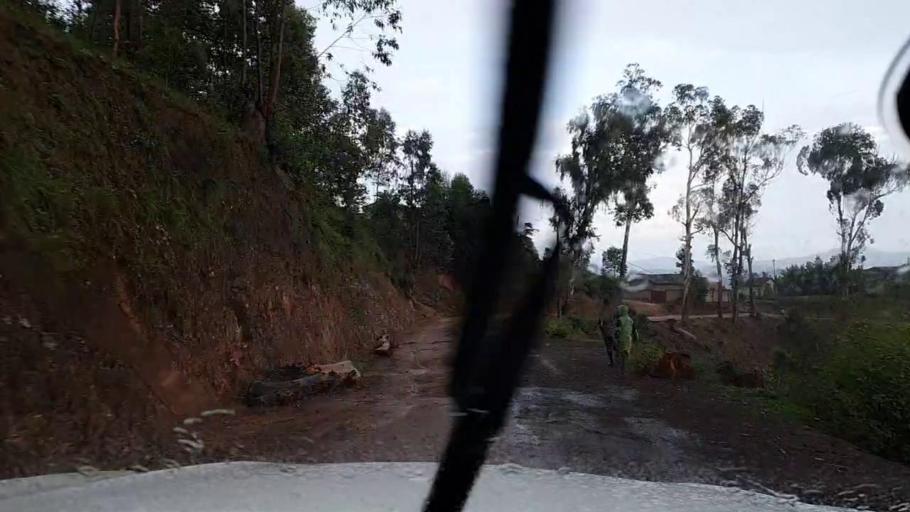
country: BI
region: Kayanza
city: Kayanza
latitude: -2.7766
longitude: 29.5355
